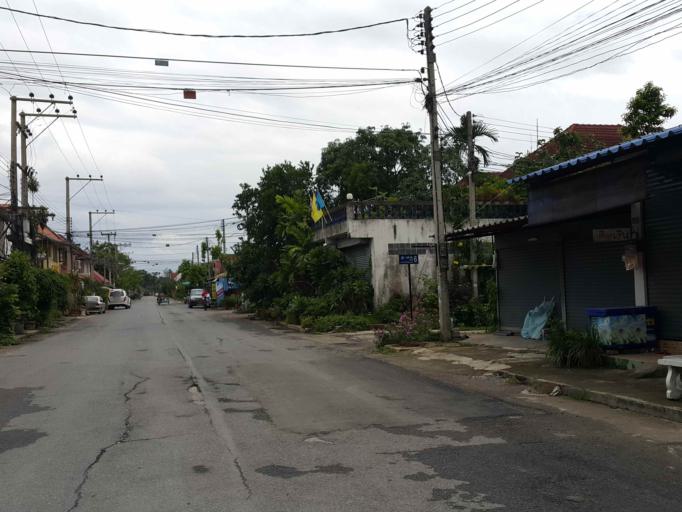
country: TH
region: Chiang Mai
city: San Sai
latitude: 18.8286
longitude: 99.0551
